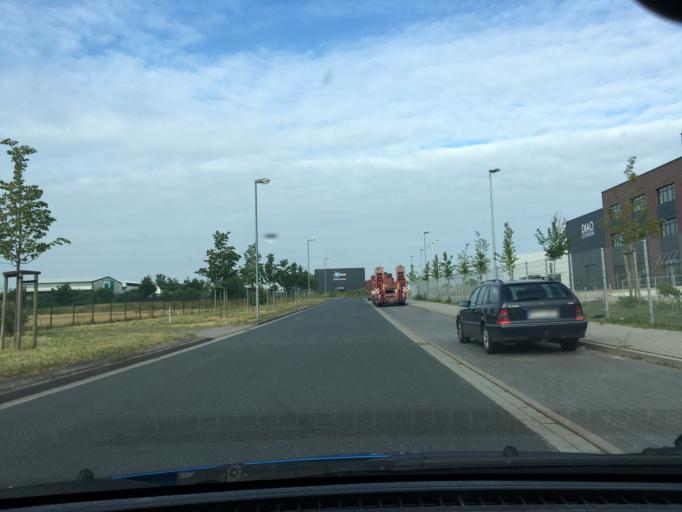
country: DE
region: Lower Saxony
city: Buchholz in der Nordheide
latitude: 53.3241
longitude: 9.8180
